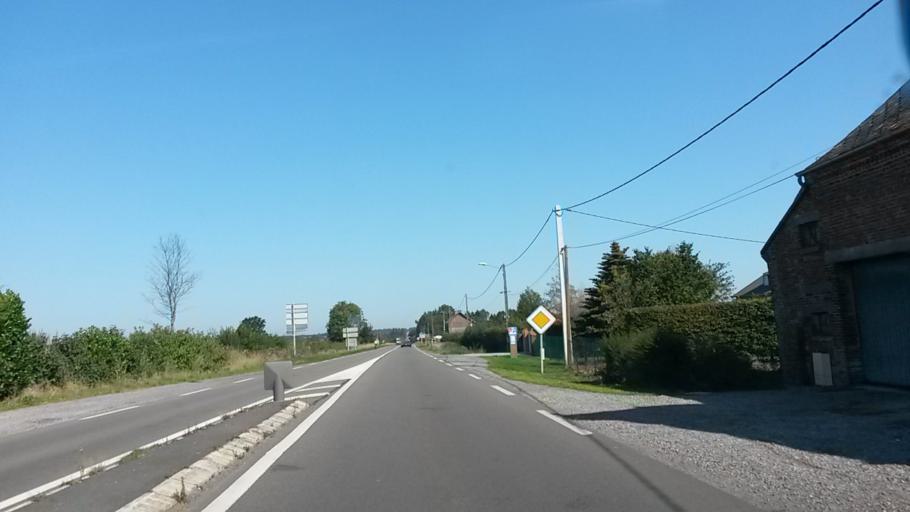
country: FR
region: Nord-Pas-de-Calais
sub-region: Departement du Nord
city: Avesnelles
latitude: 50.1553
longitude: 3.9548
